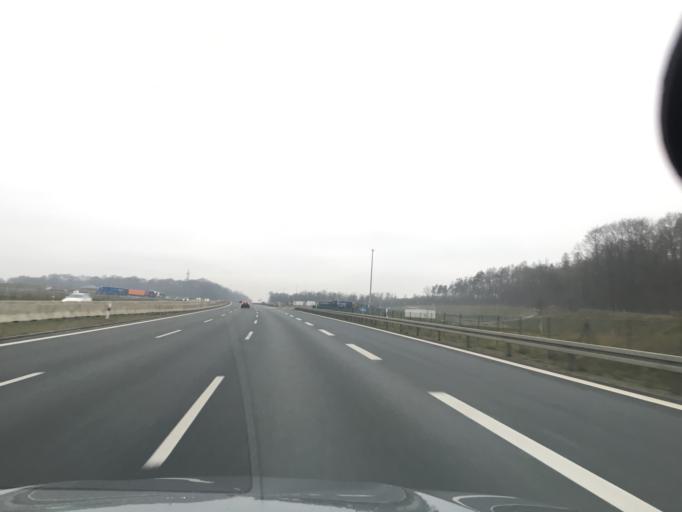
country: DE
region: Bavaria
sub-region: Regierungsbezirk Unterfranken
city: Helmstadt
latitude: 49.7755
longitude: 9.7207
